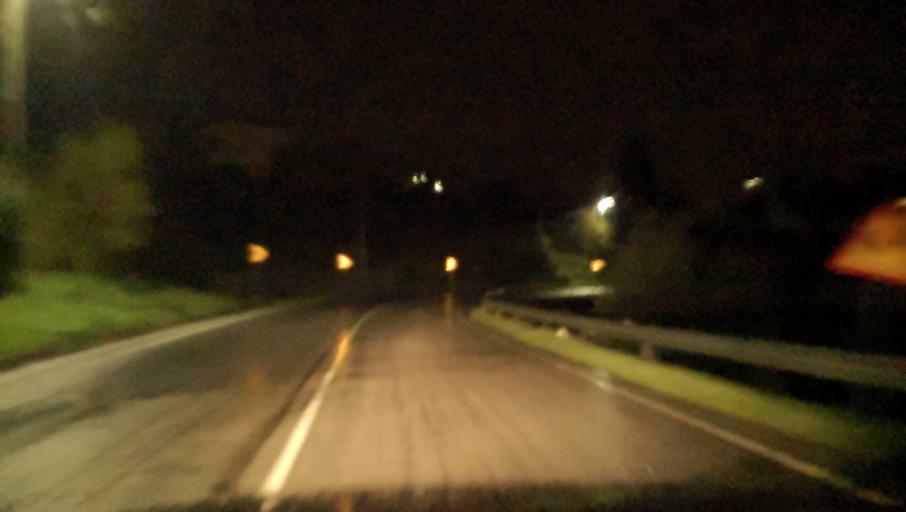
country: PT
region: Vila Real
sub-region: Vila Real
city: Vila Real
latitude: 41.3285
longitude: -7.7287
